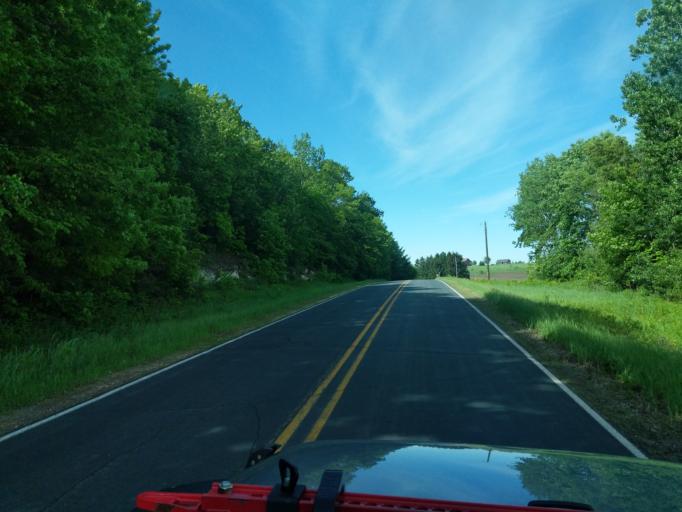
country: US
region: Wisconsin
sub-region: Saint Croix County
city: Hammond
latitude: 44.8818
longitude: -92.4873
